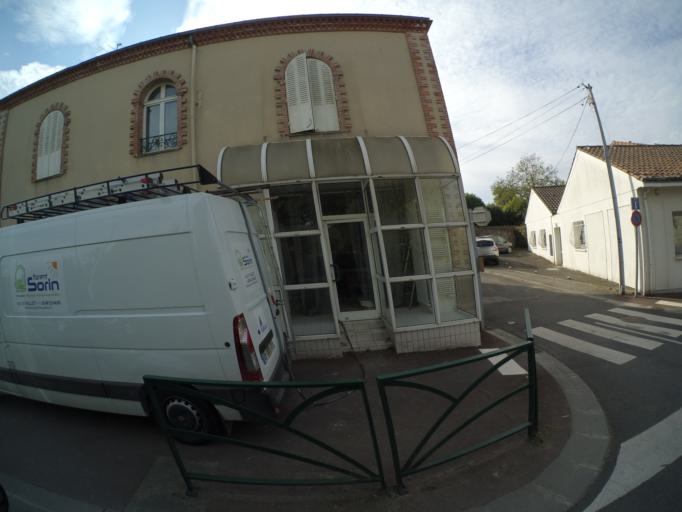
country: FR
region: Pays de la Loire
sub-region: Departement de Maine-et-Loire
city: Geste
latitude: 47.1799
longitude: -1.1098
